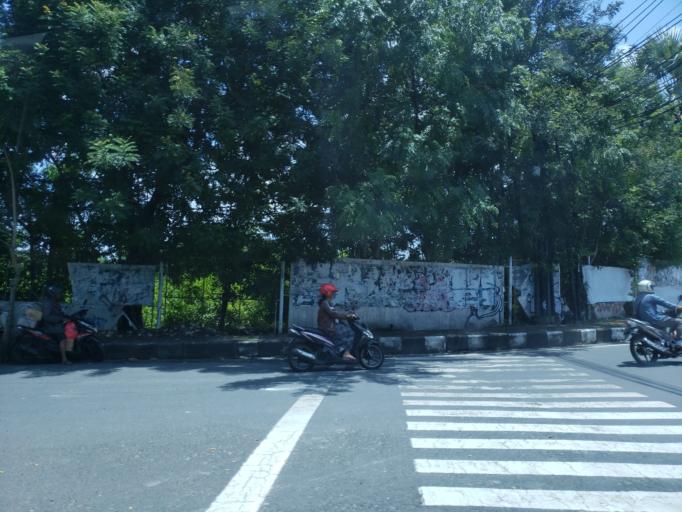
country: ID
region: Bali
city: Jimbaran
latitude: -8.7849
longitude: 115.1659
